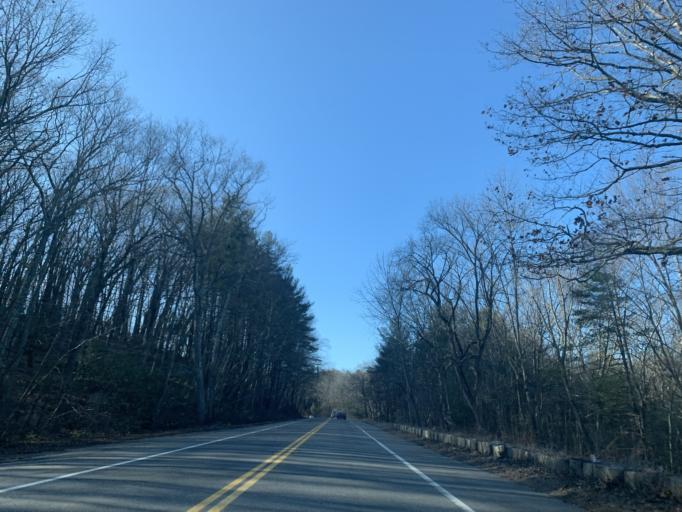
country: US
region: Massachusetts
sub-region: Middlesex County
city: Sudbury
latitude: 42.3556
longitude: -71.4707
